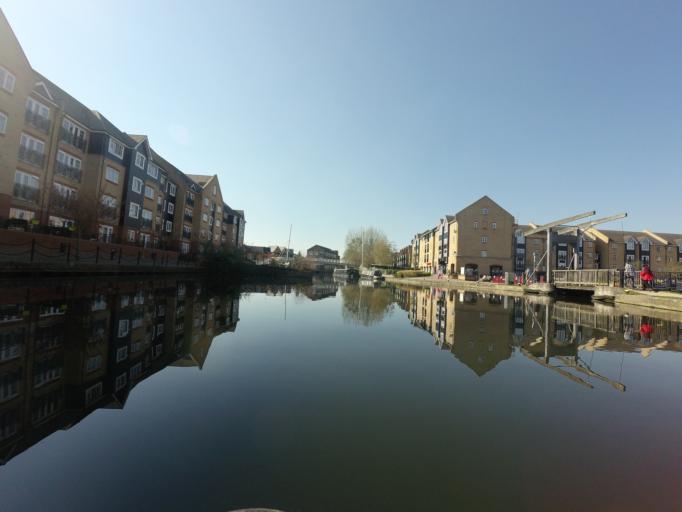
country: GB
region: England
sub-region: Hertfordshire
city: Kings Langley
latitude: 51.7329
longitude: -0.4602
